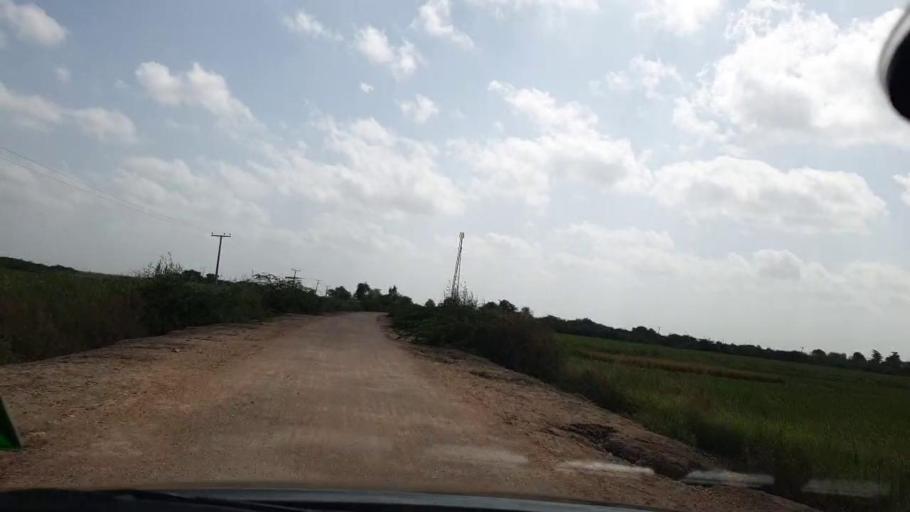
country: PK
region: Sindh
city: Kadhan
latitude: 24.5828
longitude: 69.1197
